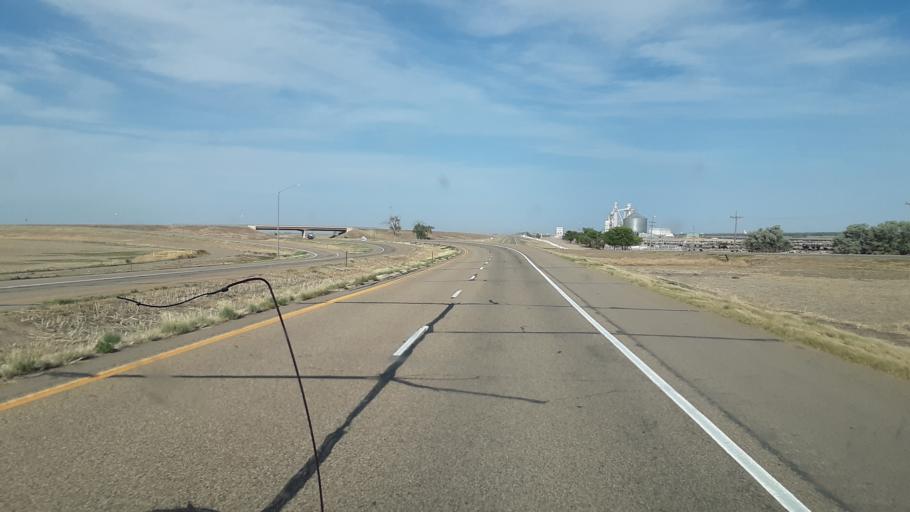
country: US
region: Colorado
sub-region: Prowers County
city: Lamar
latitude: 38.1141
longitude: -102.7291
